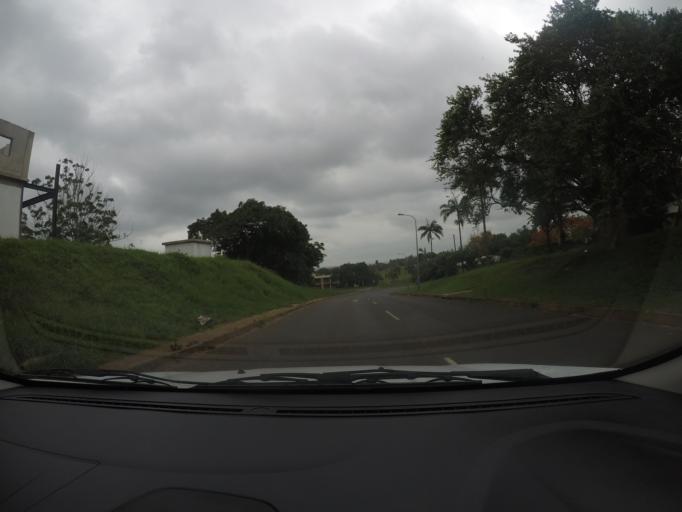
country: ZA
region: KwaZulu-Natal
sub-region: uThungulu District Municipality
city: Empangeni
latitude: -28.7465
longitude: 31.8878
